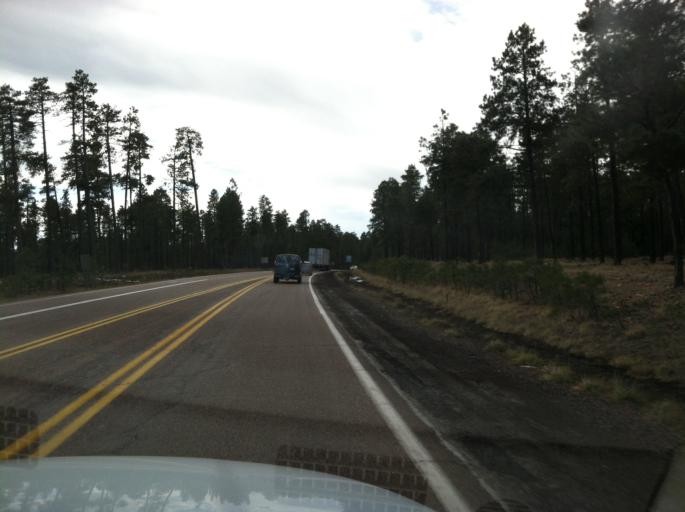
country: US
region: Arizona
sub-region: Navajo County
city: Heber-Overgaard
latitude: 34.3023
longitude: -110.8582
